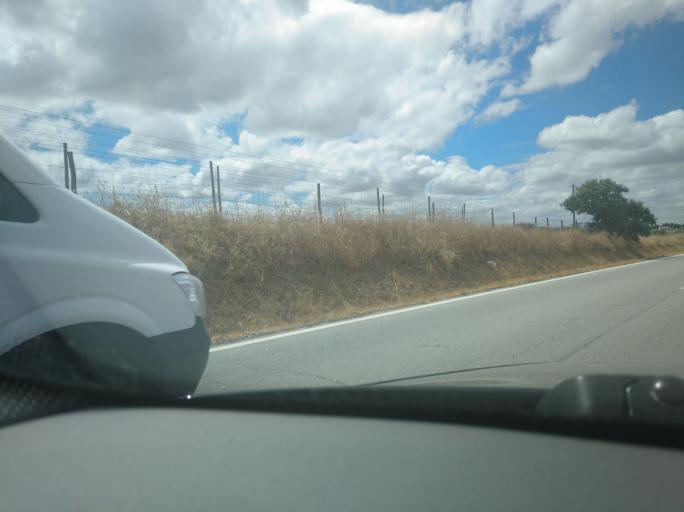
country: PT
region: Portalegre
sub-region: Arronches
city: Arronches
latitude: 39.0078
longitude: -7.2360
